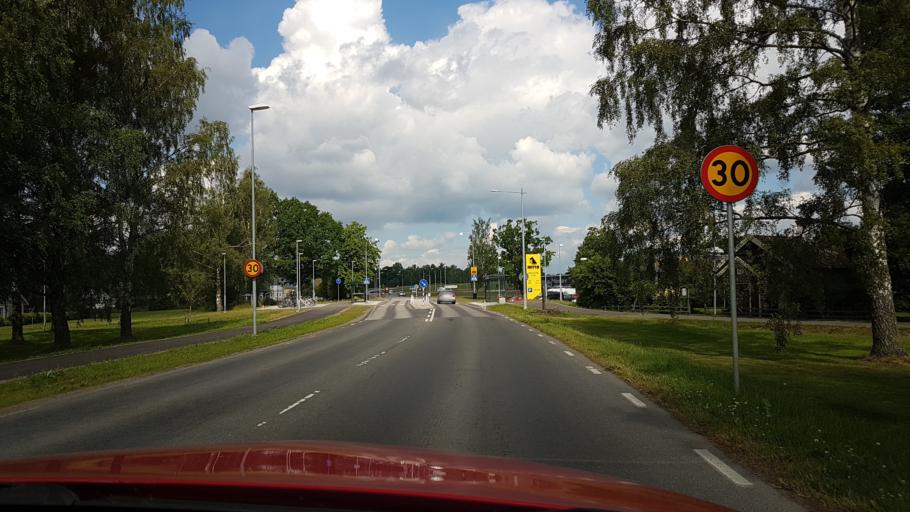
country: SE
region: Vaestra Goetaland
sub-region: Hjo Kommun
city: Hjo
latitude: 58.3116
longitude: 14.2804
